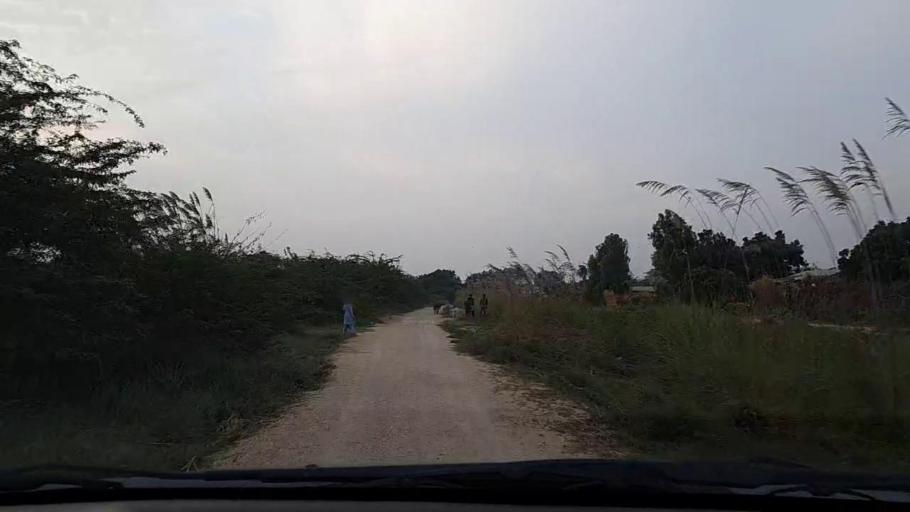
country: PK
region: Sindh
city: Thatta
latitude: 24.7707
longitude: 67.9231
